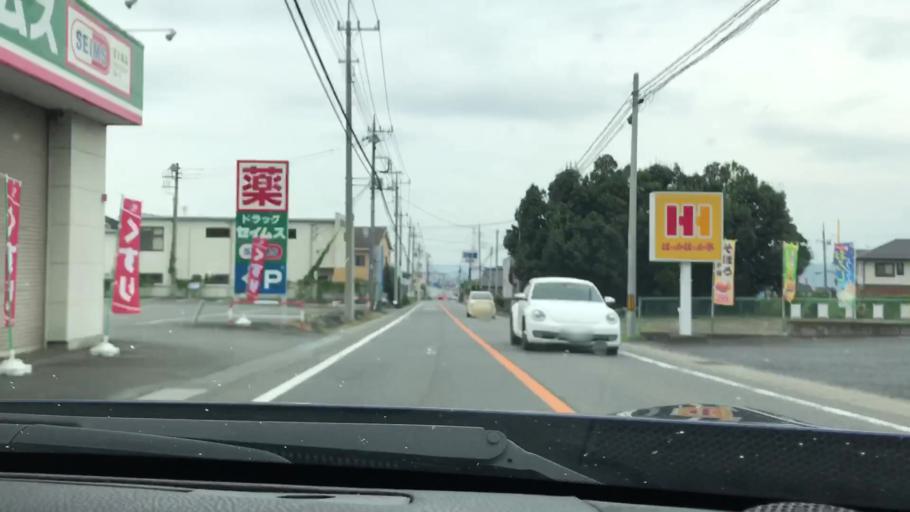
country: JP
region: Gunma
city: Kanekomachi
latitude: 36.3906
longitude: 138.9617
